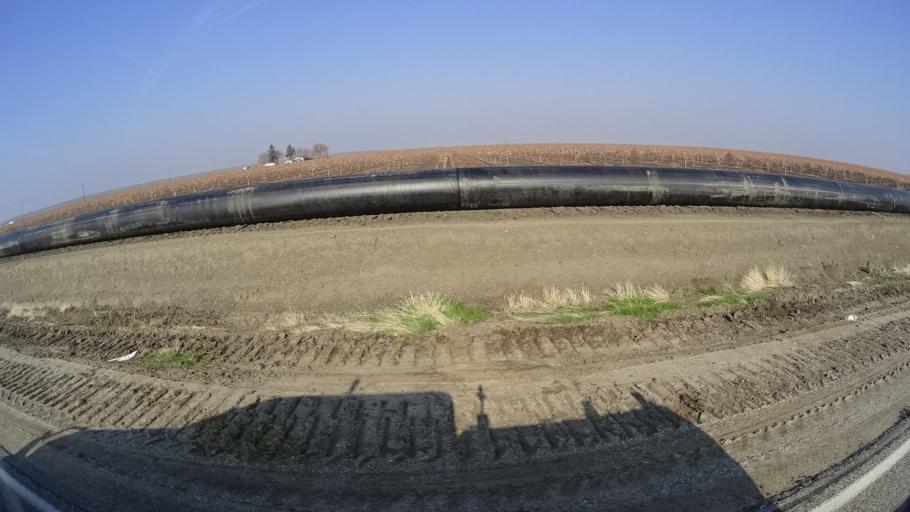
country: US
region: California
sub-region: Kern County
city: Buttonwillow
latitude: 35.3546
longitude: -119.4101
